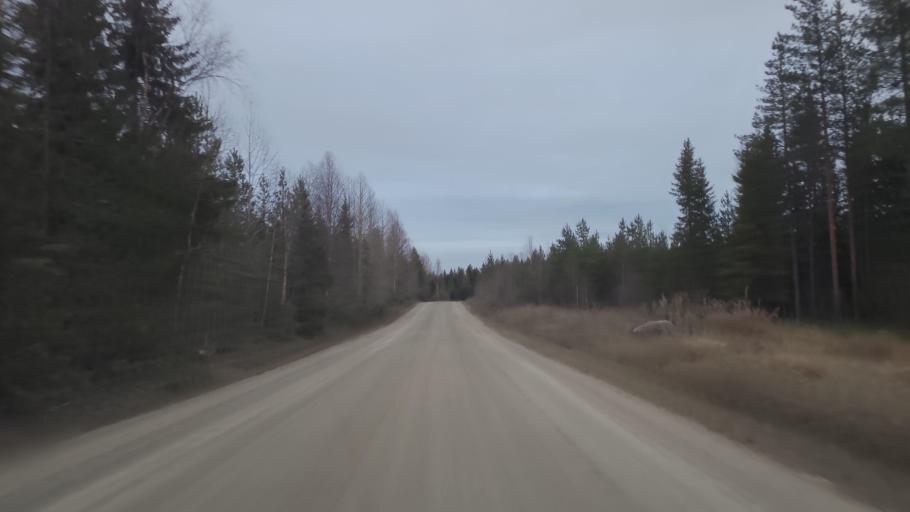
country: FI
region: Lapland
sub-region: Kemi-Tornio
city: Tervola
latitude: 66.0710
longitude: 24.8817
